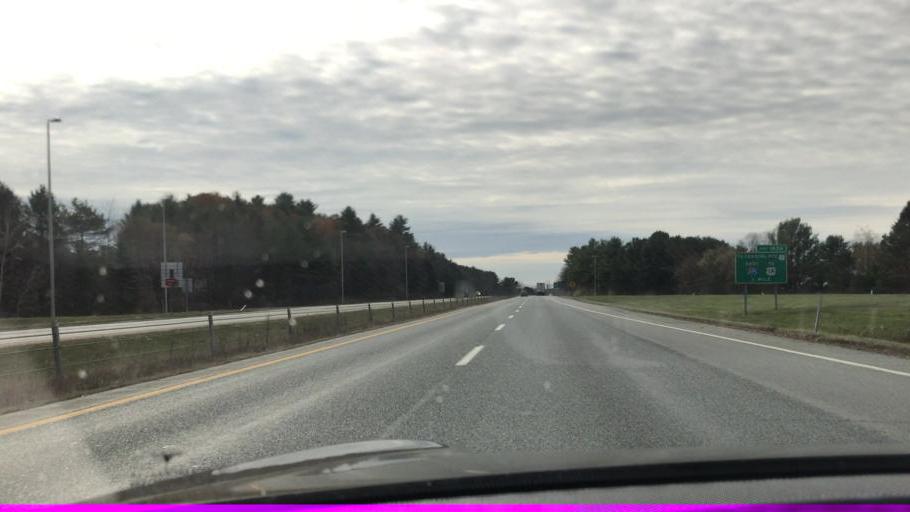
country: US
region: Maine
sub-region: Penobscot County
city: Bangor
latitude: 44.7975
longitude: -68.8025
